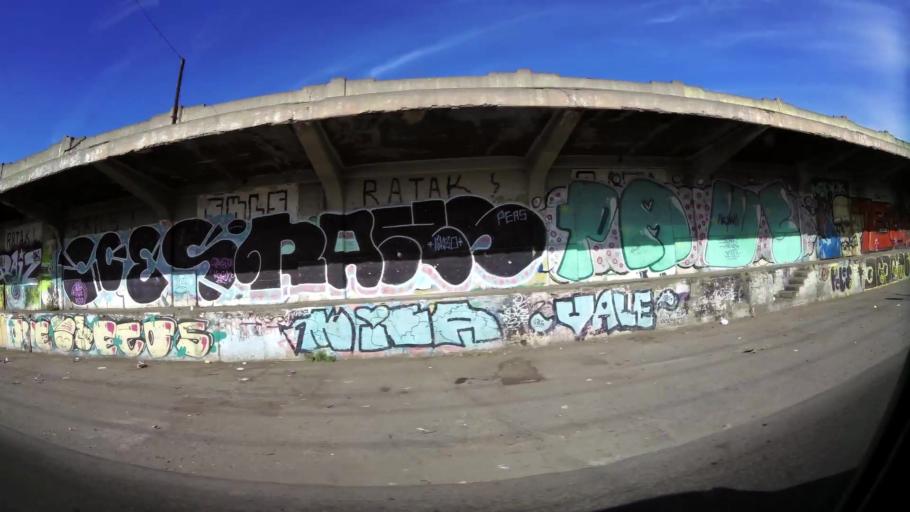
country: CL
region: Santiago Metropolitan
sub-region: Provincia de Santiago
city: Santiago
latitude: -33.4613
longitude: -70.6804
